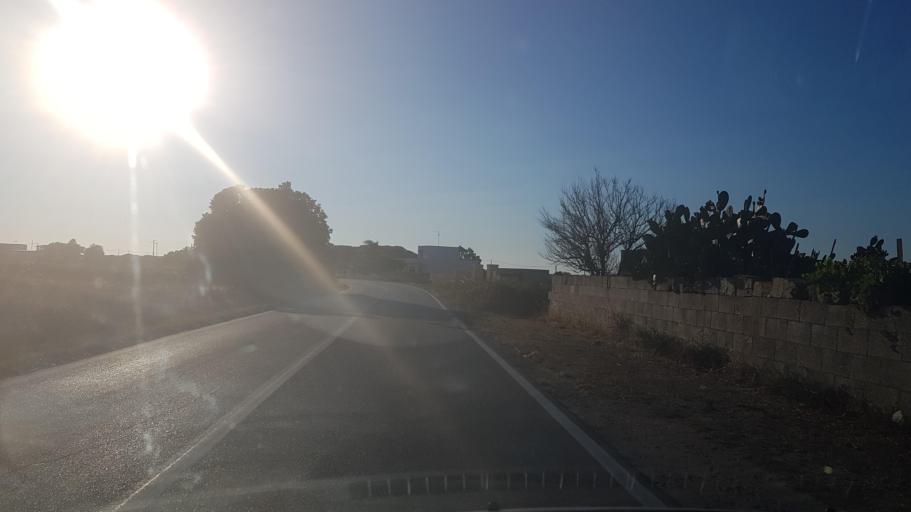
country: IT
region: Apulia
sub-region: Provincia di Lecce
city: Struda
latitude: 40.3260
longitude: 18.3164
